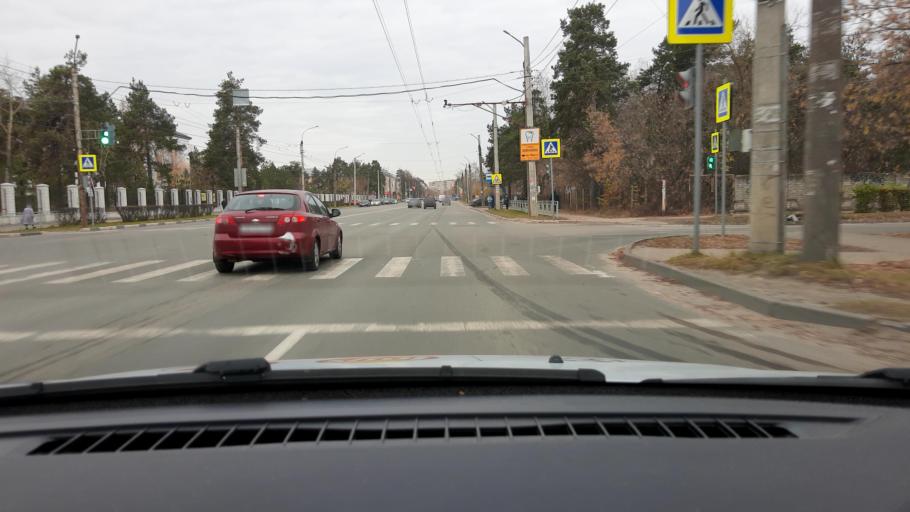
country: RU
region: Nizjnij Novgorod
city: Dzerzhinsk
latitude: 56.2478
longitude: 43.4446
